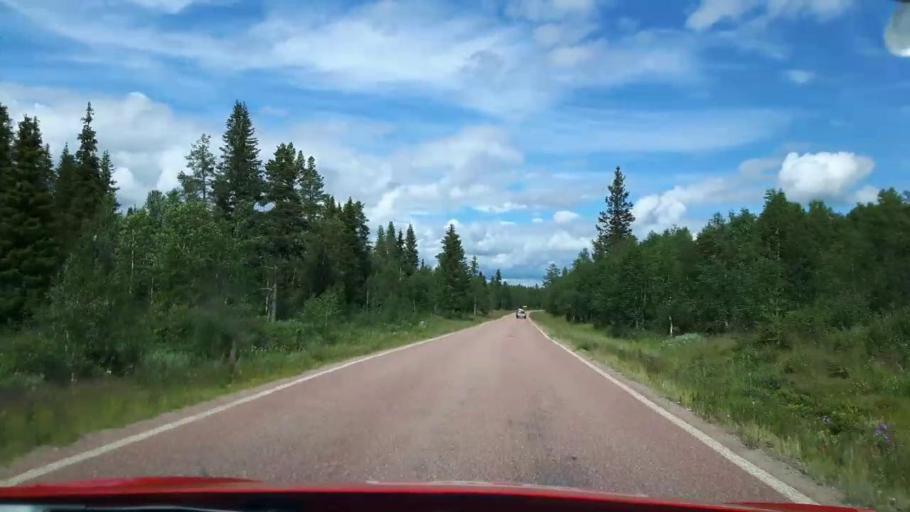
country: NO
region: Hedmark
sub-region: Trysil
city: Innbygda
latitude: 62.0068
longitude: 12.9755
